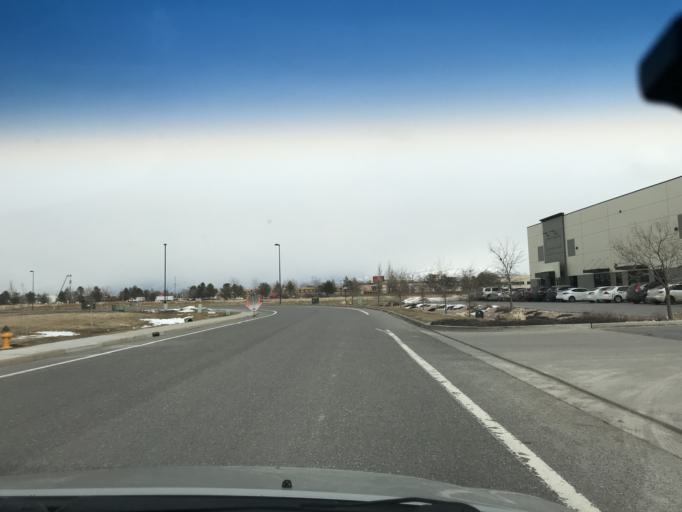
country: US
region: Utah
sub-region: Salt Lake County
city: West Valley City
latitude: 40.7729
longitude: -112.0282
